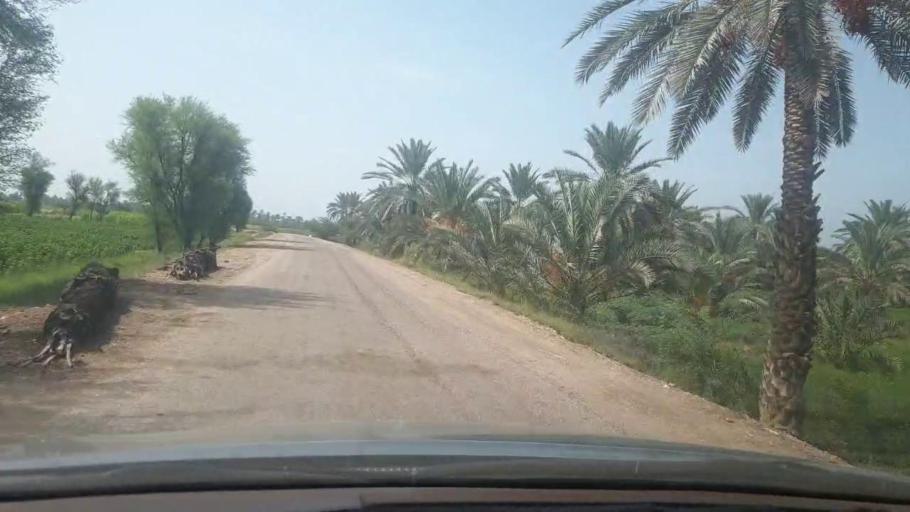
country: PK
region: Sindh
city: Ranipur
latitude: 27.2654
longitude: 68.5817
